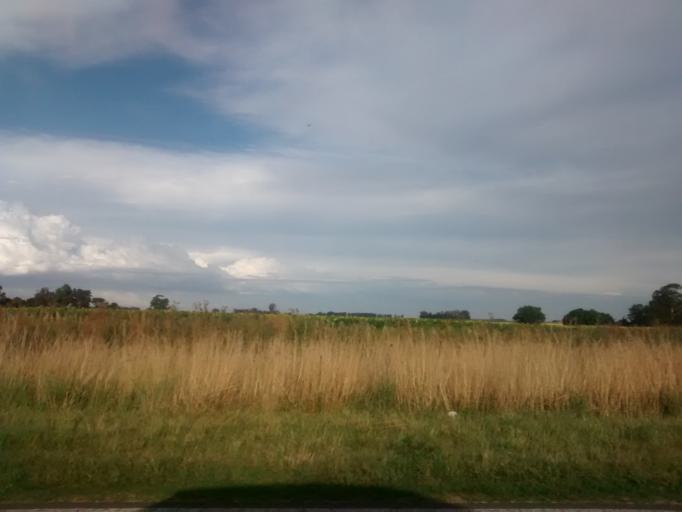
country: AR
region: Buenos Aires
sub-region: Partido de Loberia
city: Loberia
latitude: -38.2153
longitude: -58.7320
